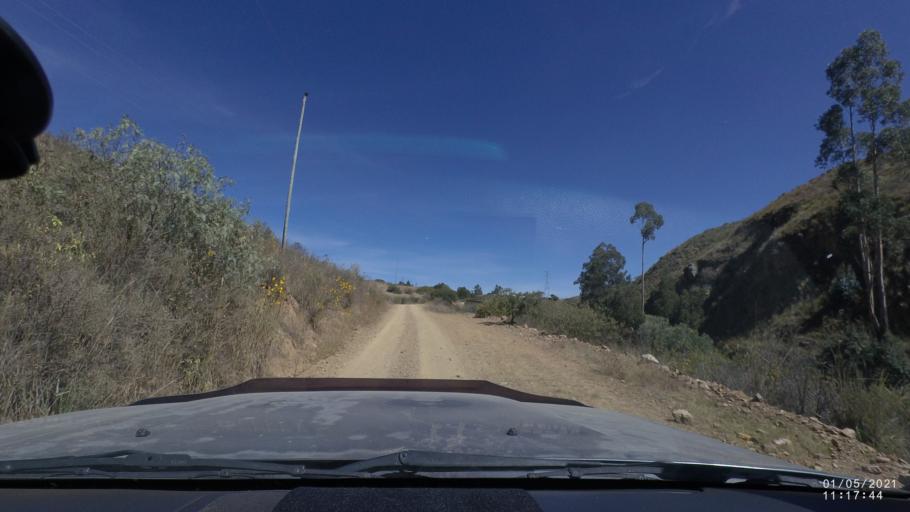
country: BO
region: Cochabamba
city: Tarata
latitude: -17.6400
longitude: -66.1149
